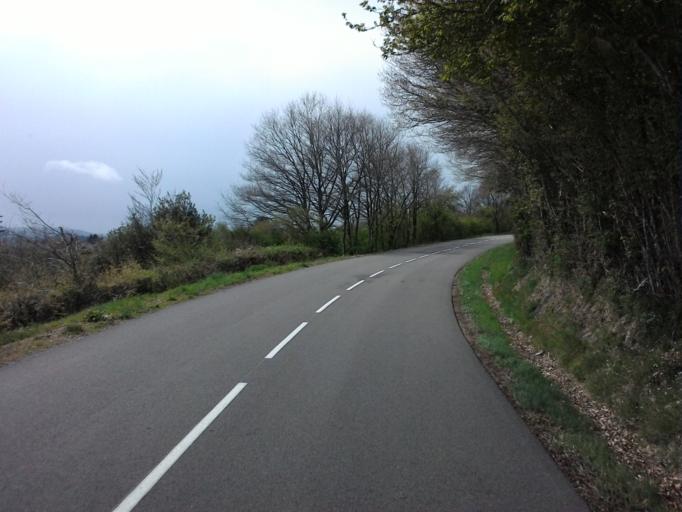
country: FR
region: Bourgogne
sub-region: Departement de la Cote-d'Or
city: Saulieu
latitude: 47.1804
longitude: 4.0888
